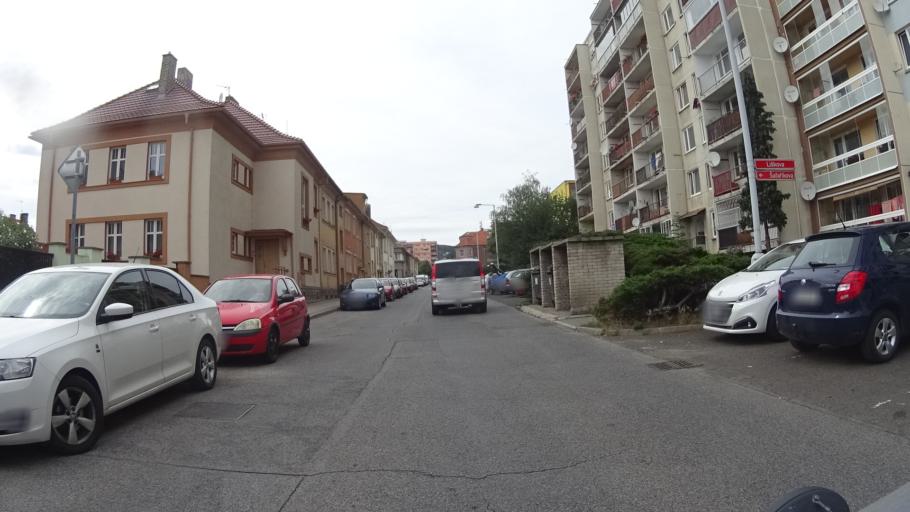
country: CZ
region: Ustecky
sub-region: Okres Litomerice
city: Litomerice
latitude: 50.5372
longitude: 14.1235
